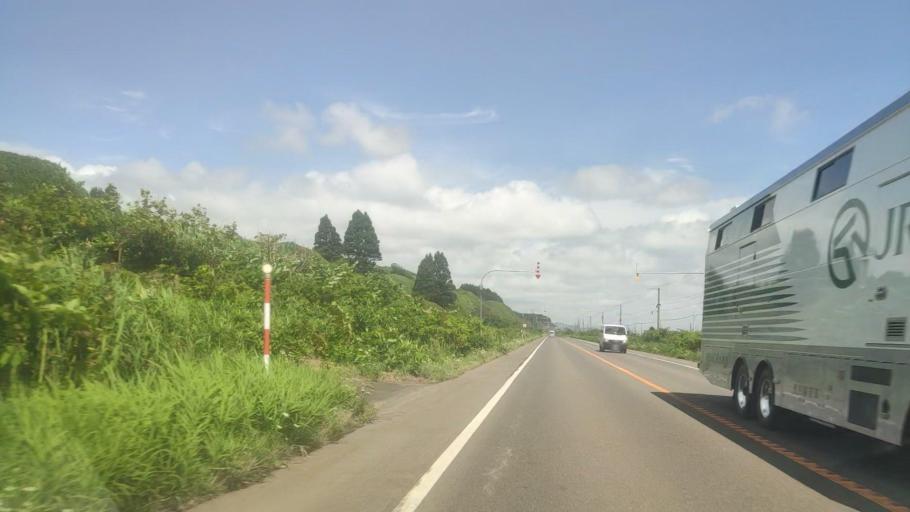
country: JP
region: Hokkaido
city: Niseko Town
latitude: 42.3444
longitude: 140.2818
